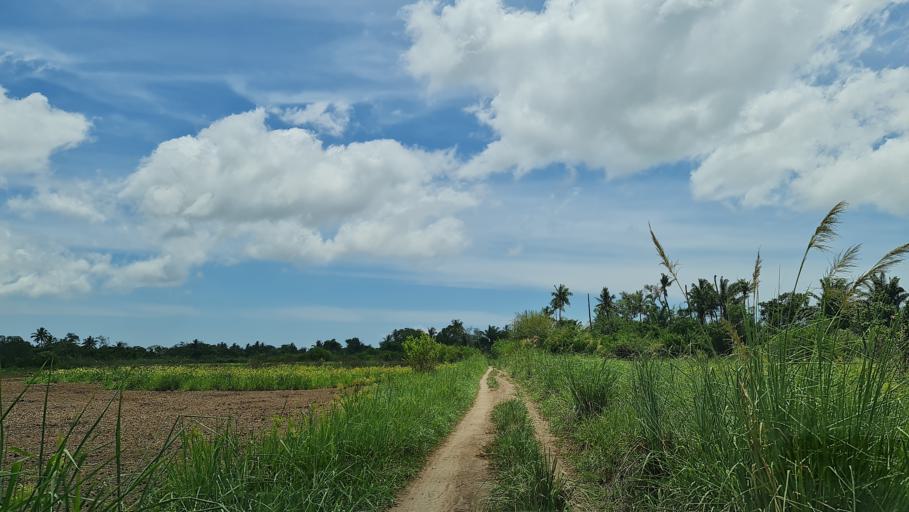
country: MZ
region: Zambezia
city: Quelimane
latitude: -17.5847
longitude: 37.3867
